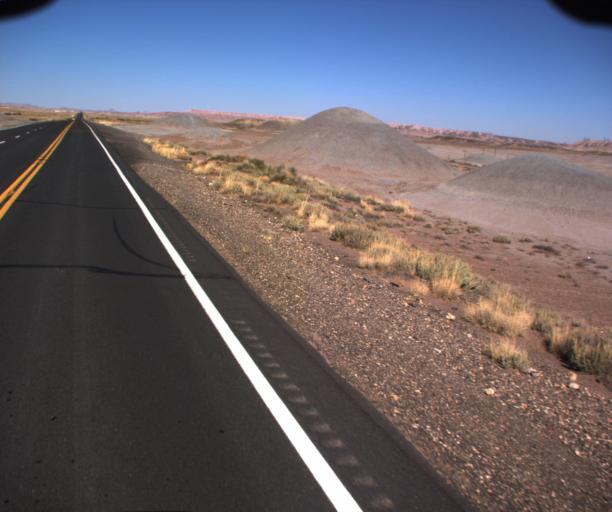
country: US
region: Arizona
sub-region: Coconino County
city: Tuba City
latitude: 35.9309
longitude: -111.4012
